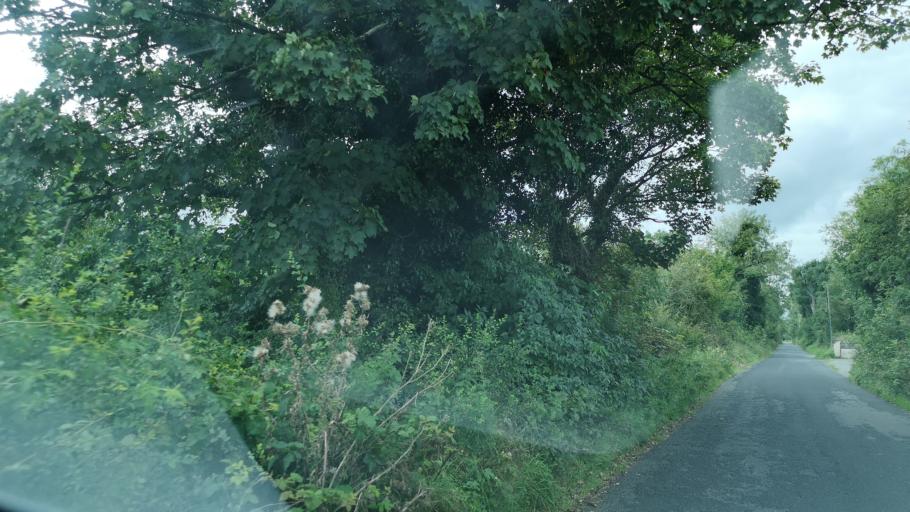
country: IE
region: Connaught
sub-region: County Galway
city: Loughrea
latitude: 53.1574
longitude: -8.4535
